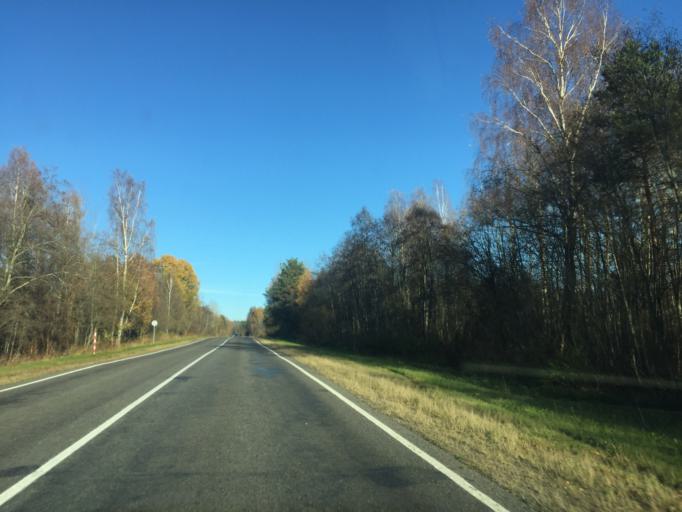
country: BY
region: Vitebsk
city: Dzisna
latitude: 55.3641
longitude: 28.3576
